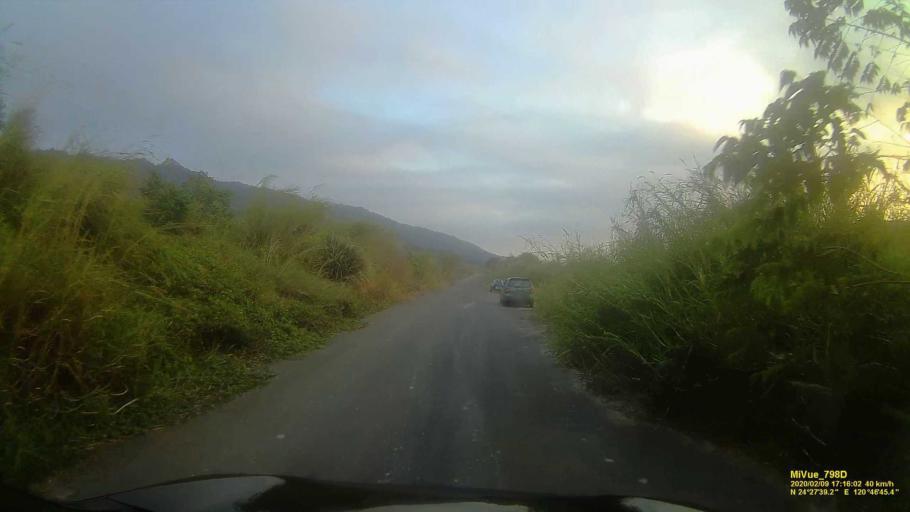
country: TW
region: Taiwan
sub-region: Miaoli
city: Miaoli
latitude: 24.4608
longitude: 120.7793
